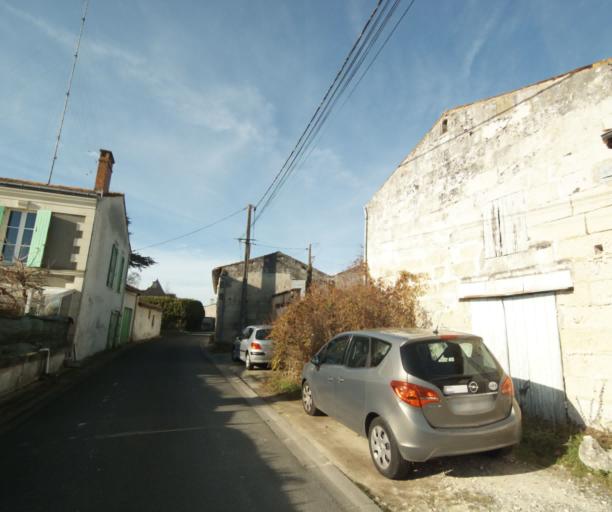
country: FR
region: Poitou-Charentes
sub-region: Departement de la Charente-Maritime
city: Chaniers
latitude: 45.7281
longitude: -0.5849
